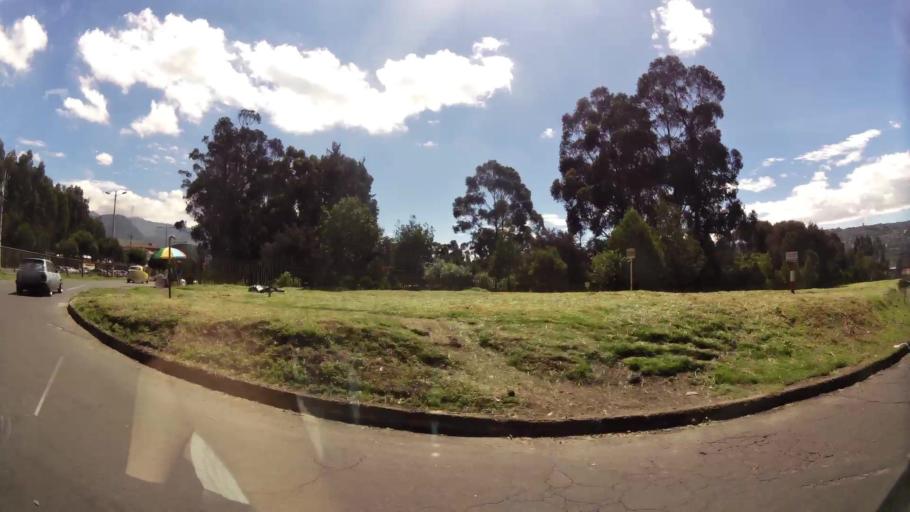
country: EC
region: Pichincha
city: Quito
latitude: -0.2895
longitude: -78.5501
